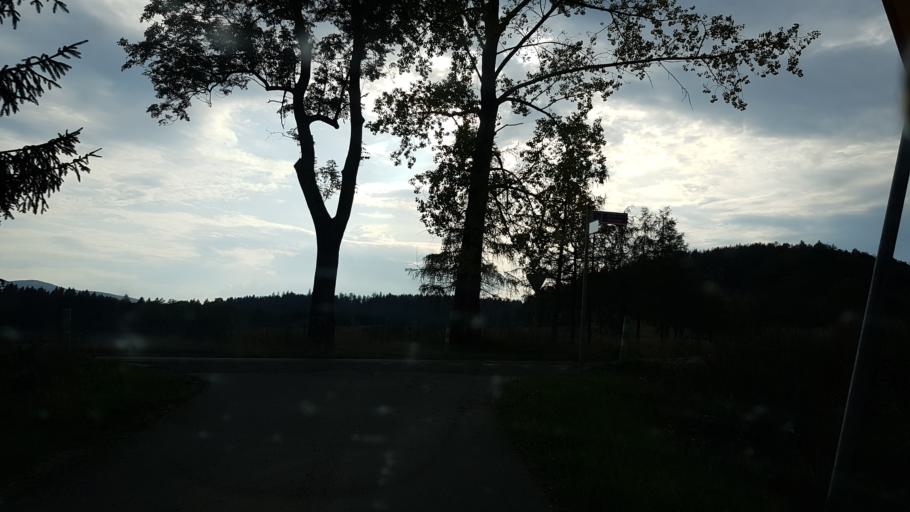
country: PL
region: Lower Silesian Voivodeship
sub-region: Powiat kamiennogorski
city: Marciszow
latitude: 50.8808
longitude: 15.9979
